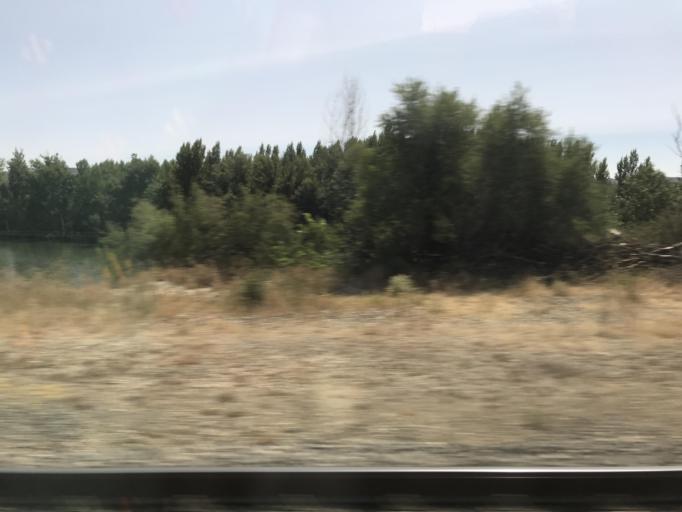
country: ES
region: Castille and Leon
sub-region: Provincia de Palencia
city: Soto de Cerrato
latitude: 41.9507
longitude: -4.4580
